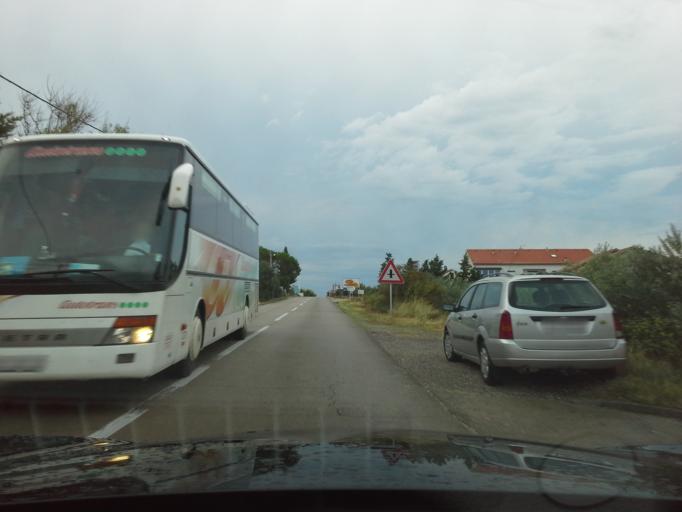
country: HR
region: Primorsko-Goranska
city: Banjol
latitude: 44.7384
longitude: 14.8018
